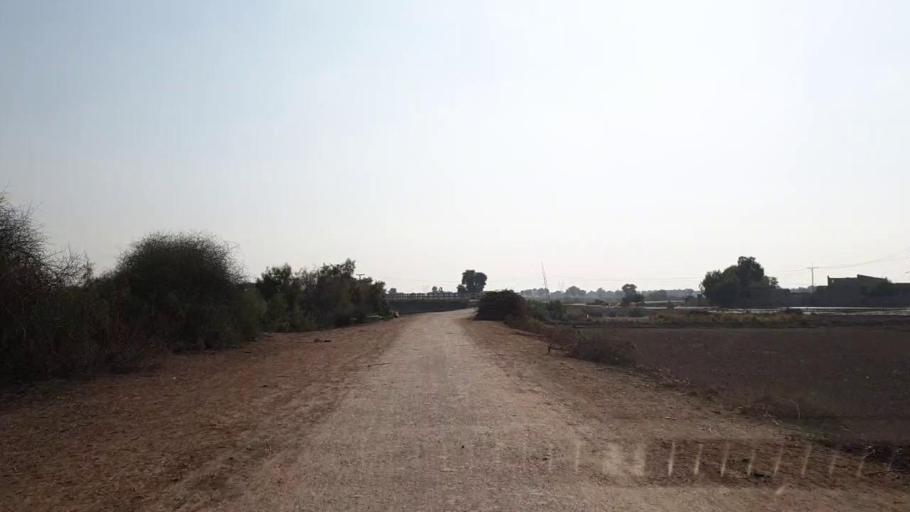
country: PK
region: Sindh
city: Sehwan
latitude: 26.4436
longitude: 67.8096
